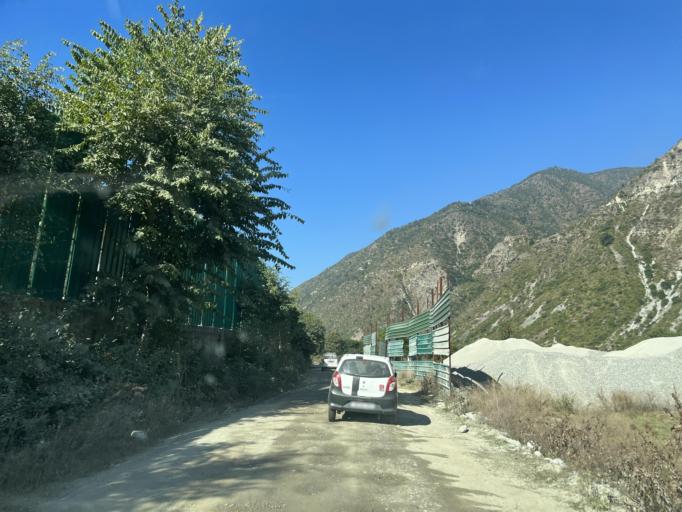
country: IN
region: Uttarakhand
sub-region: Almora
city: Ranikhet
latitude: 29.5521
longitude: 79.3988
